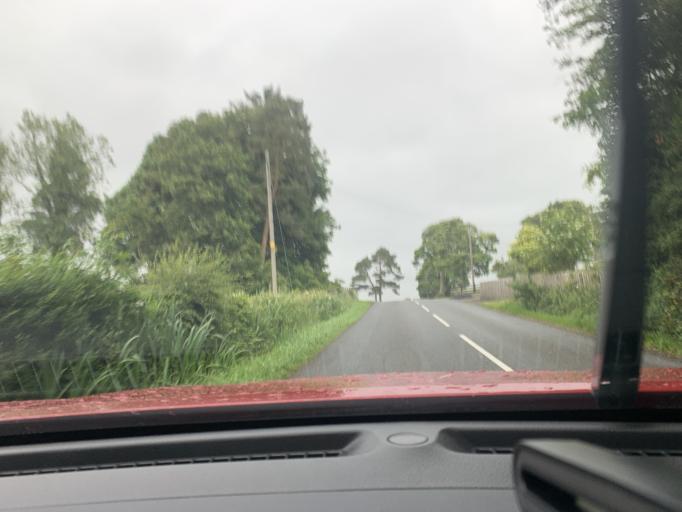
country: GB
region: Northern Ireland
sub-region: Fermanagh District
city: Enniskillen
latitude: 54.3124
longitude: -7.6835
